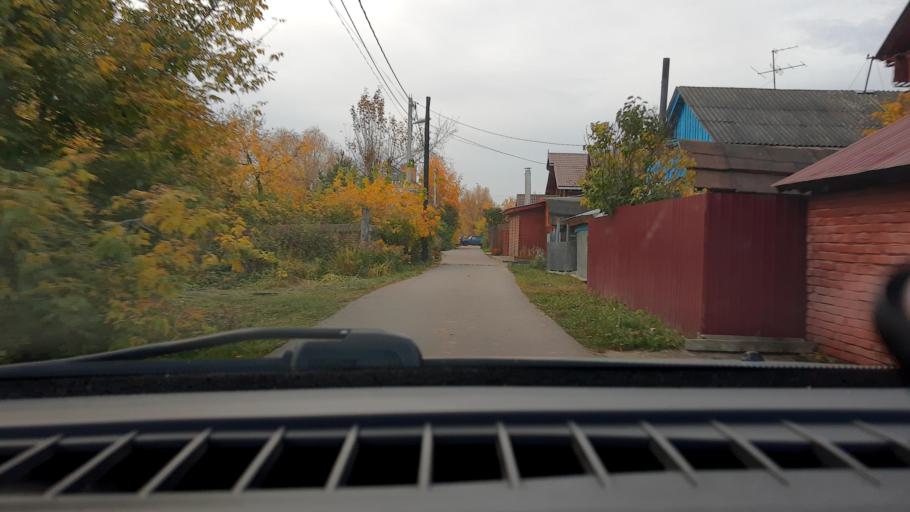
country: RU
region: Nizjnij Novgorod
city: Afonino
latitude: 56.2923
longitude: 44.1033
